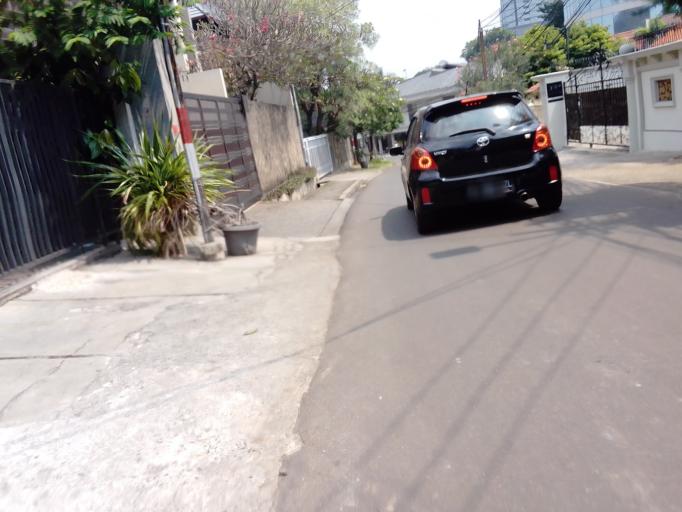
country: ID
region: Jakarta Raya
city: Jakarta
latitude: -6.2309
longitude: 106.8109
